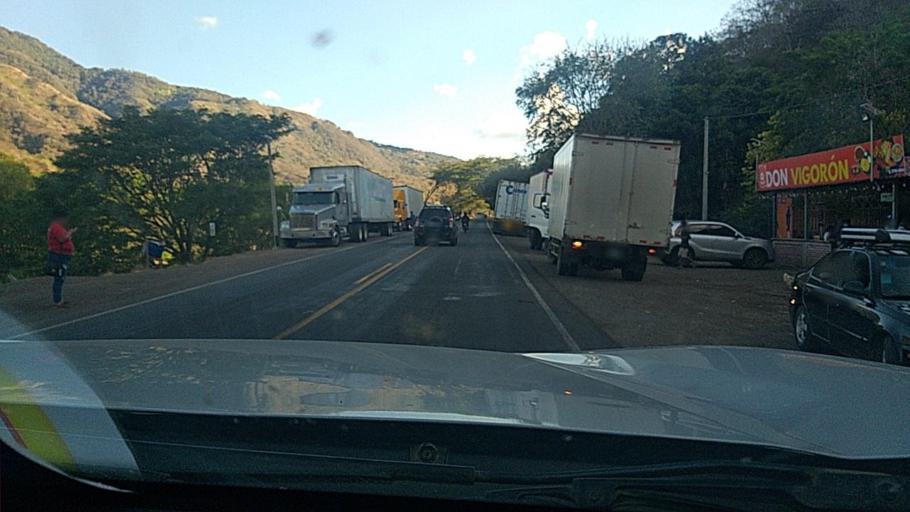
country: NI
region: Esteli
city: Condega
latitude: 13.2921
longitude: -86.3473
